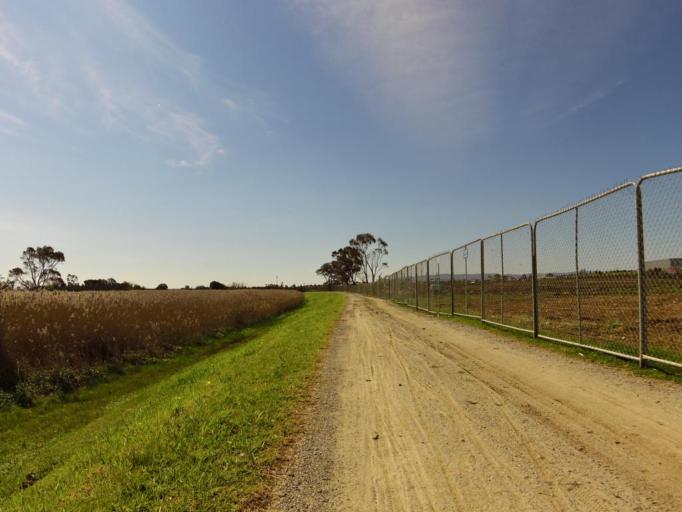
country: AU
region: Victoria
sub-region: Greater Dandenong
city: Keysborough
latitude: -38.0313
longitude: 145.1855
